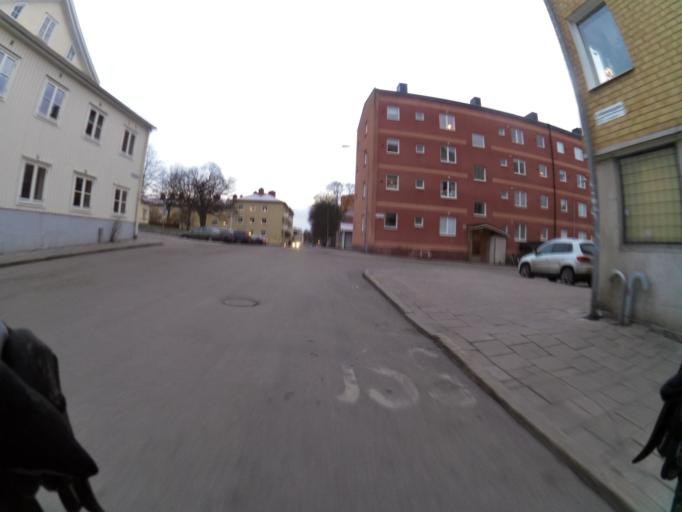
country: SE
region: Gaevleborg
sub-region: Gavle Kommun
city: Gavle
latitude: 60.6716
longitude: 17.1483
